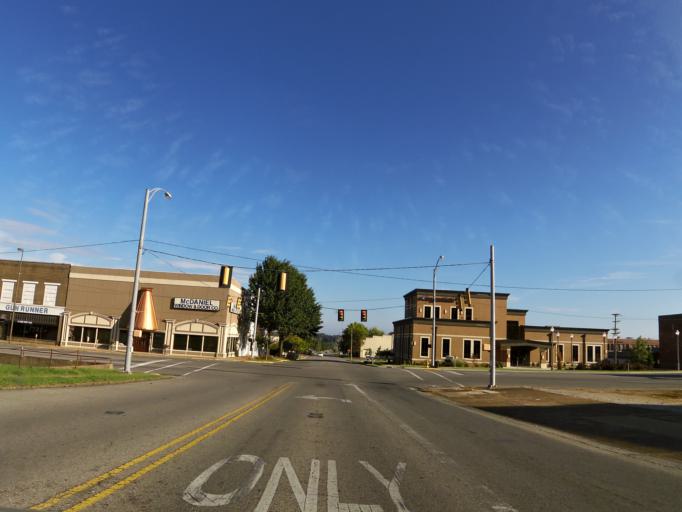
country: US
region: Alabama
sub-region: Lauderdale County
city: Florence
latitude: 34.8016
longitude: -87.6735
